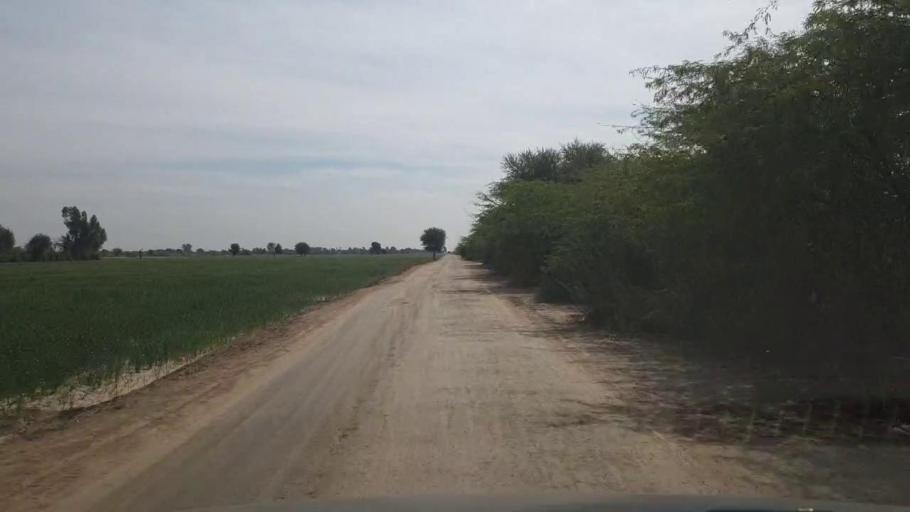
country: PK
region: Sindh
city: Kunri
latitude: 25.2831
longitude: 69.5953
